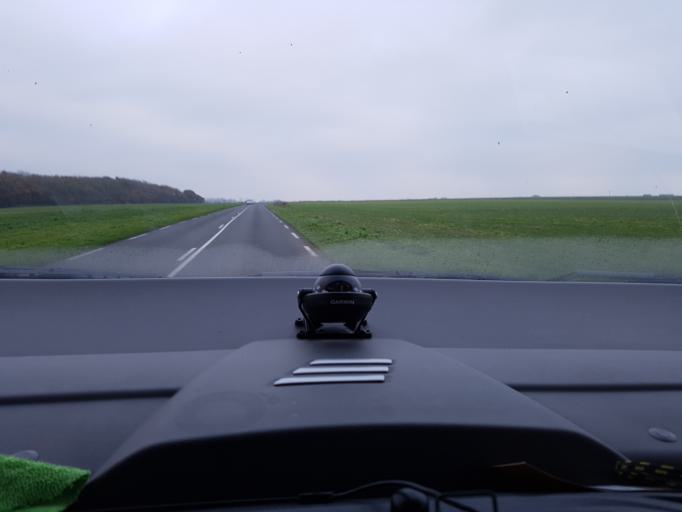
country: FR
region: Picardie
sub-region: Departement de la Somme
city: Ault
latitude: 50.1095
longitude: 1.4771
